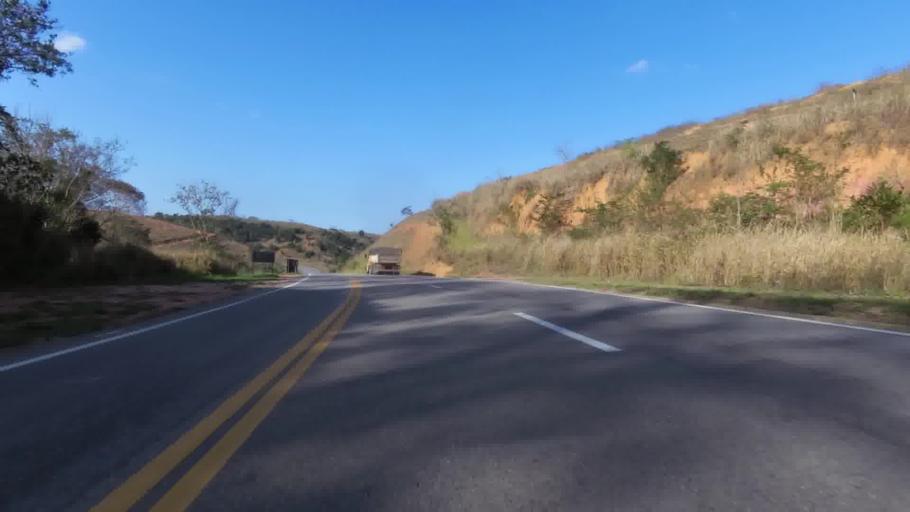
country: BR
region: Espirito Santo
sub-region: Mimoso Do Sul
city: Mimoso do Sul
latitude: -21.2185
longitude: -41.3006
